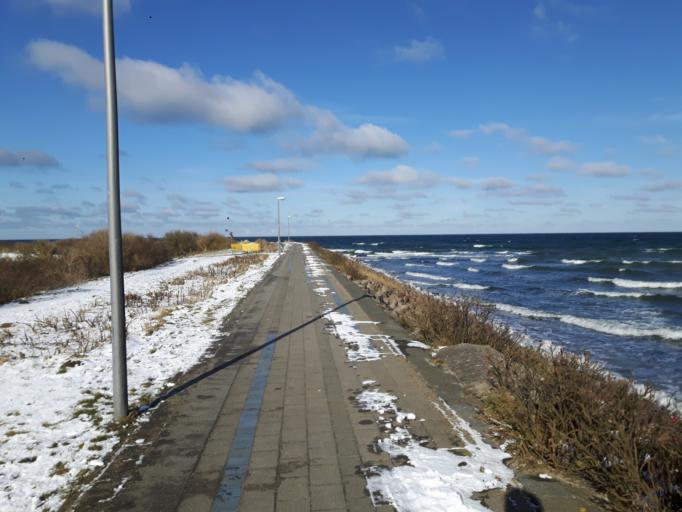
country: DE
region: Schleswig-Holstein
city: Heiligenhafen
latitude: 54.3836
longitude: 10.9527
